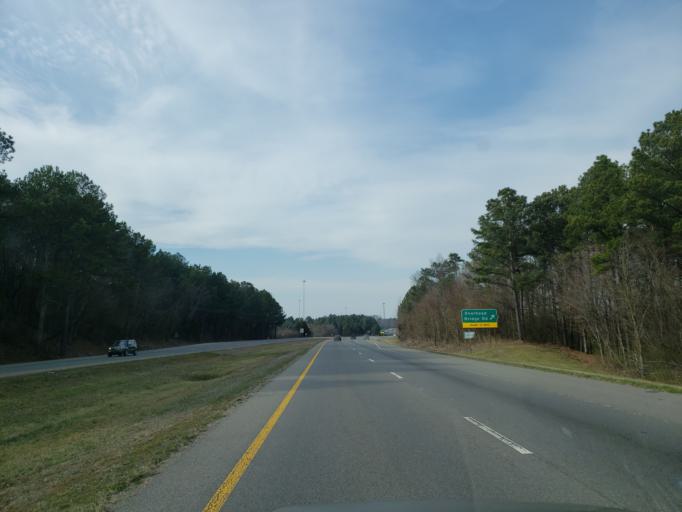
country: US
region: Tennessee
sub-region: Bradley County
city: East Cleveland
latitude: 35.1623
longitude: -84.8465
